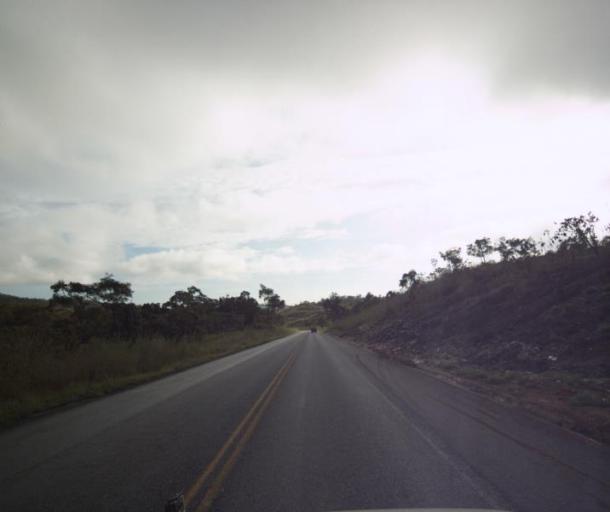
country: BR
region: Goias
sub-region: Pirenopolis
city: Pirenopolis
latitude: -15.7203
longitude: -48.6973
